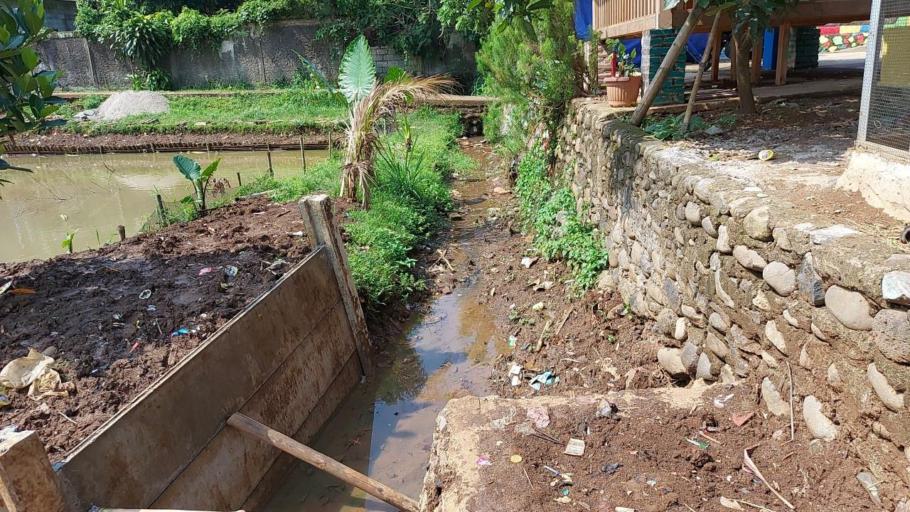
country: ID
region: West Java
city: Cibinong
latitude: -6.5120
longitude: 106.7842
